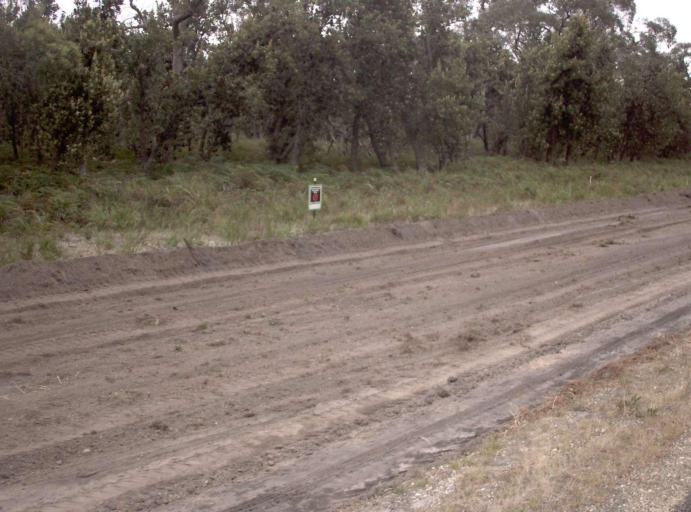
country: AU
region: Victoria
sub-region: East Gippsland
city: Bairnsdale
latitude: -38.0725
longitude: 147.5457
